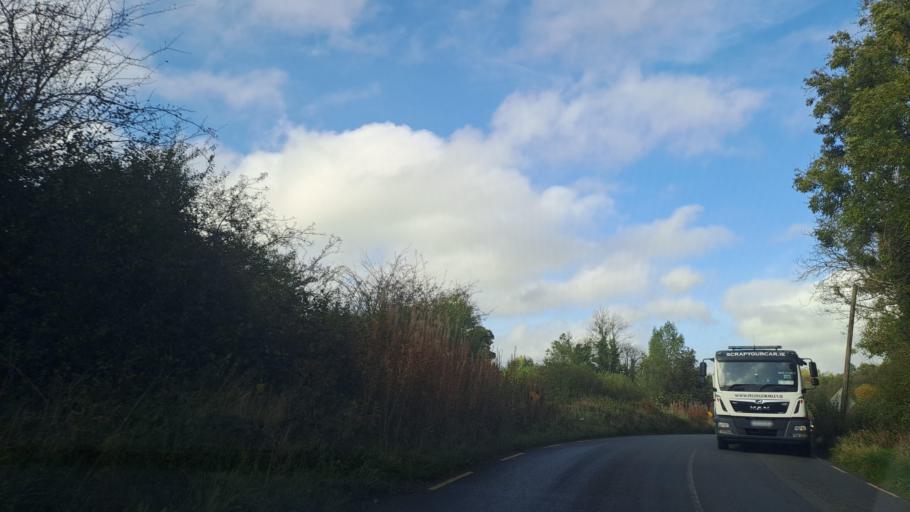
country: IE
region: Ulster
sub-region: An Cabhan
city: Cootehill
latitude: 54.0359
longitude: -6.9720
